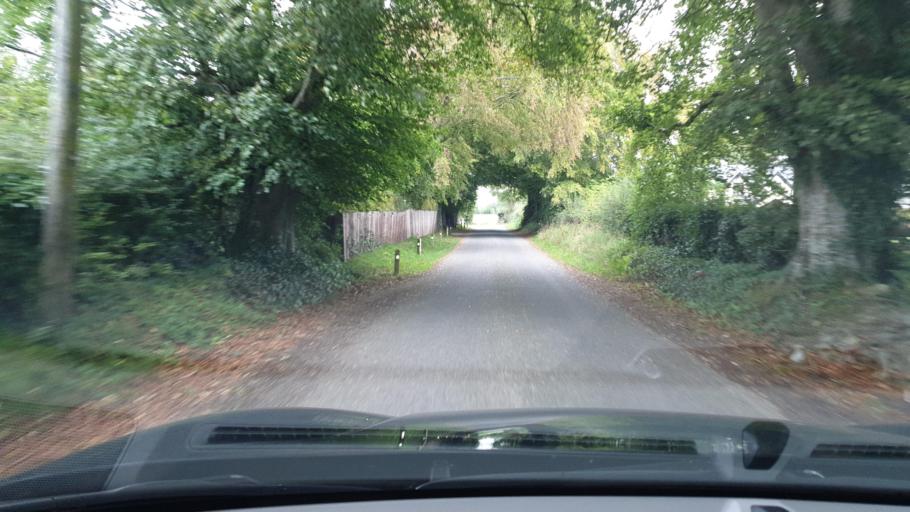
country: IE
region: Leinster
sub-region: An Mhi
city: Dunshaughlin
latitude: 53.5614
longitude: -6.5137
